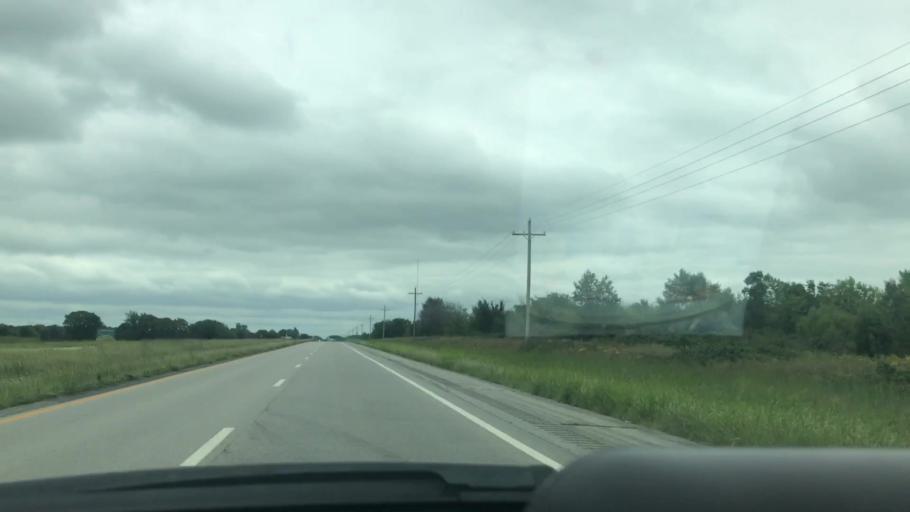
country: US
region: Oklahoma
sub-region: Mayes County
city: Pryor
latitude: 36.4129
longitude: -95.2804
